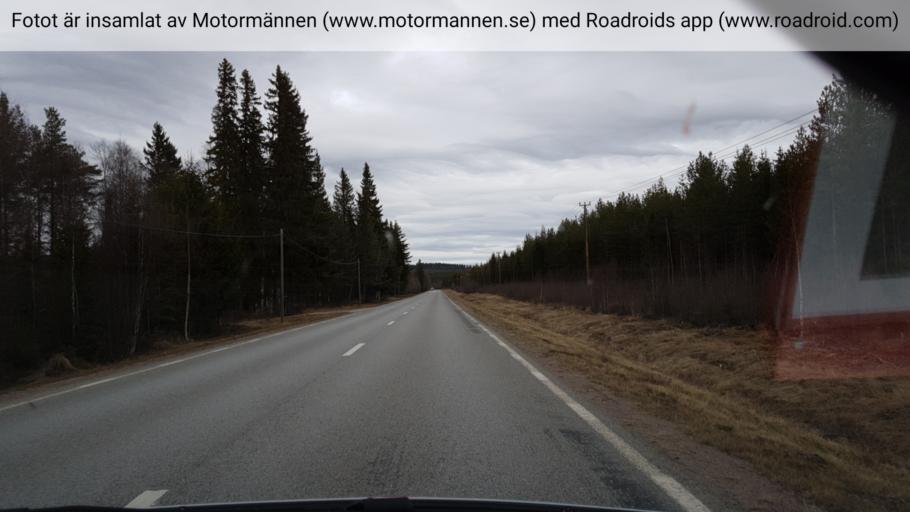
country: SE
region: Vaesternorrland
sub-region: Solleftea Kommun
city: As
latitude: 63.7054
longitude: 16.9303
